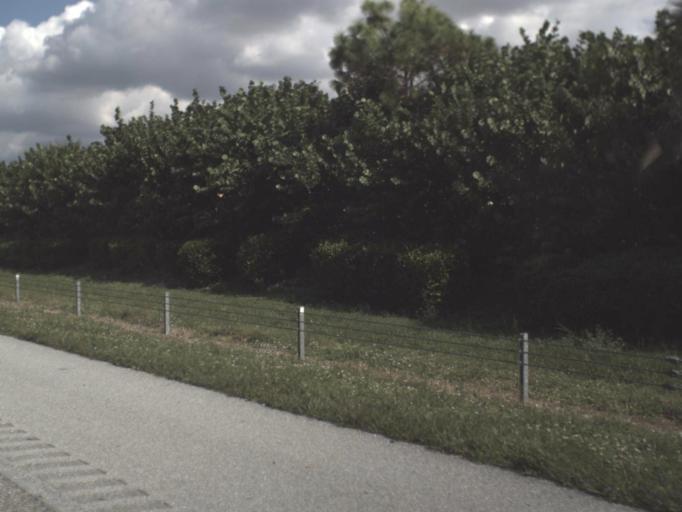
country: US
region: Florida
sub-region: Palm Beach County
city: Greenacres City
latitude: 26.6002
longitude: -80.1734
